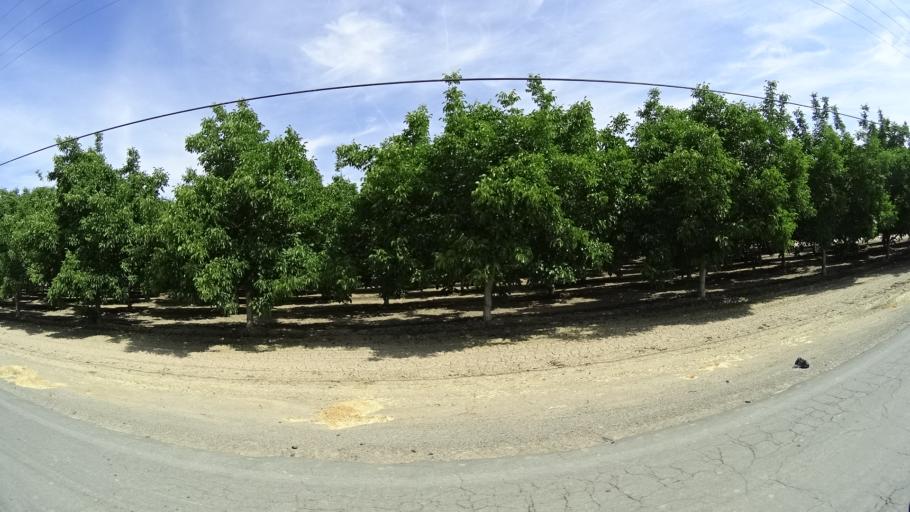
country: US
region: California
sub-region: Kings County
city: Hanford
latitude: 36.3570
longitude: -119.6017
